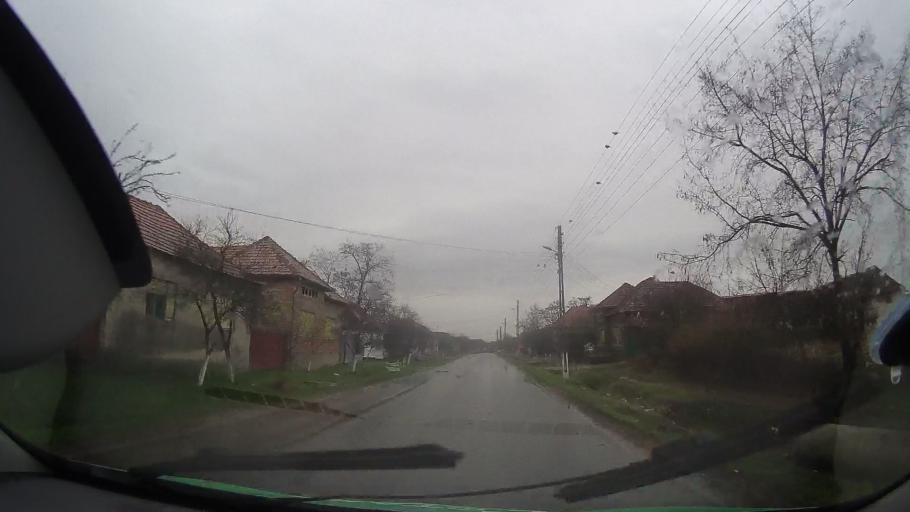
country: RO
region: Bihor
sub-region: Comuna Olcea
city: Olcea
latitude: 46.6849
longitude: 21.9860
